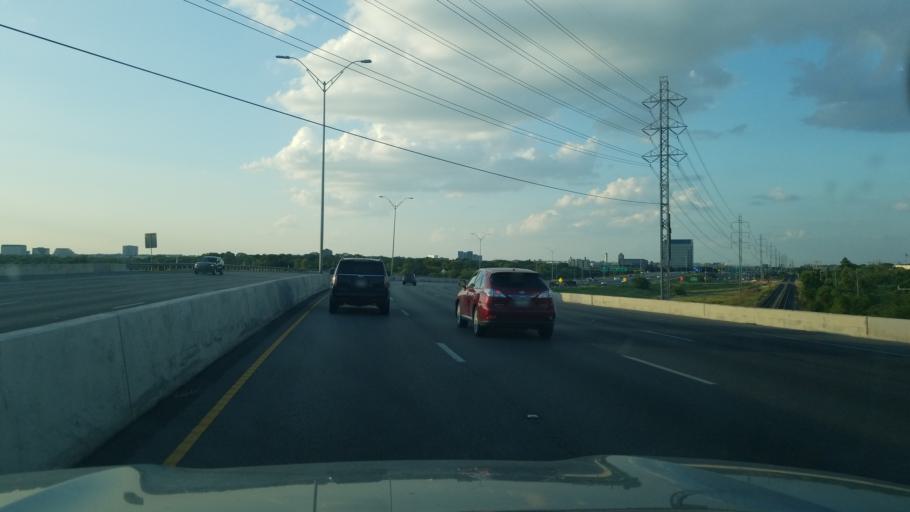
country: US
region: Texas
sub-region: Bexar County
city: Olmos Park
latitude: 29.4948
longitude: -98.4841
